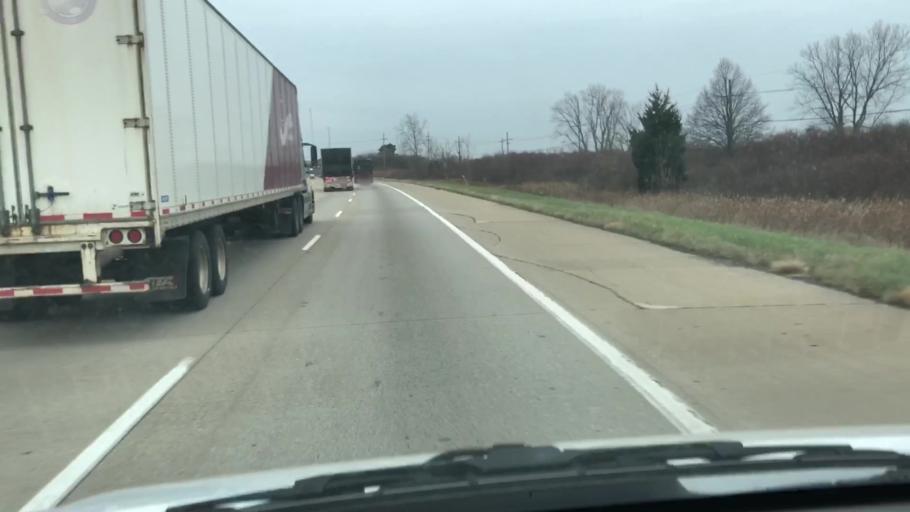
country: US
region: Michigan
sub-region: Monroe County
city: South Rockwood
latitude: 42.0399
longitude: -83.2852
